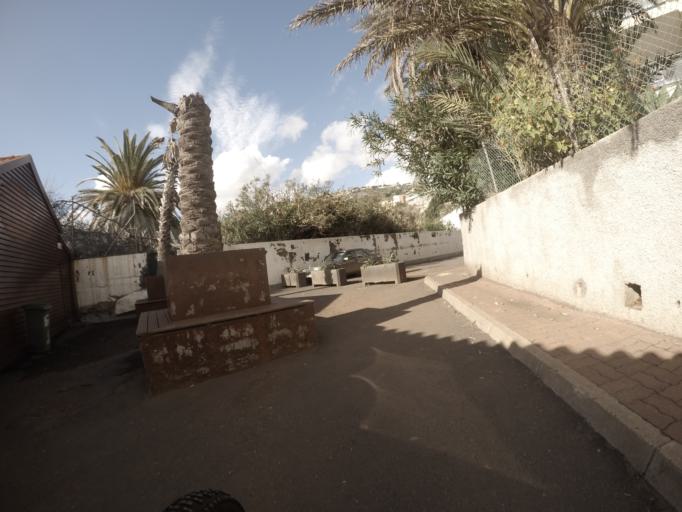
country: PT
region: Madeira
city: Camara de Lobos
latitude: 32.6390
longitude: -16.9506
